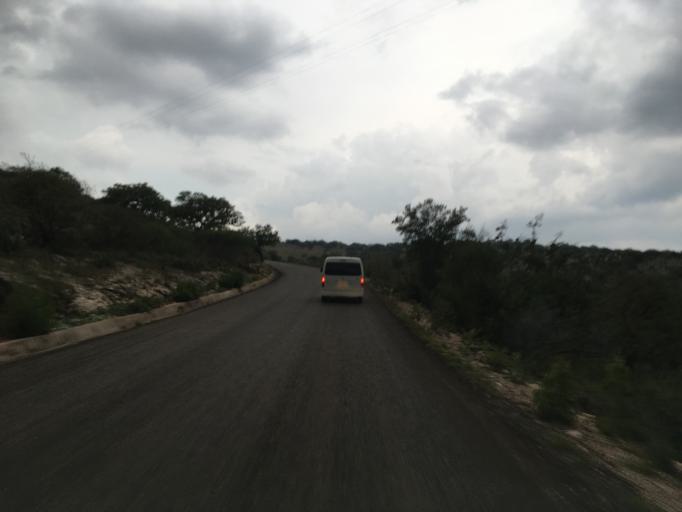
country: MX
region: Oaxaca
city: Magdalena Jaltepec
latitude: 17.2962
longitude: -97.2730
